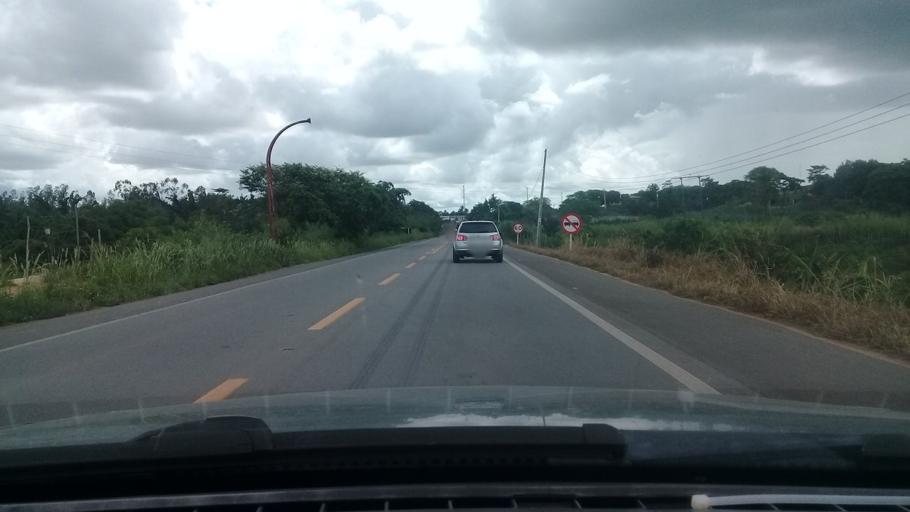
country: BR
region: Pernambuco
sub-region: Nazare Da Mata
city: Nazare da Mata
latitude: -7.7588
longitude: -35.2336
